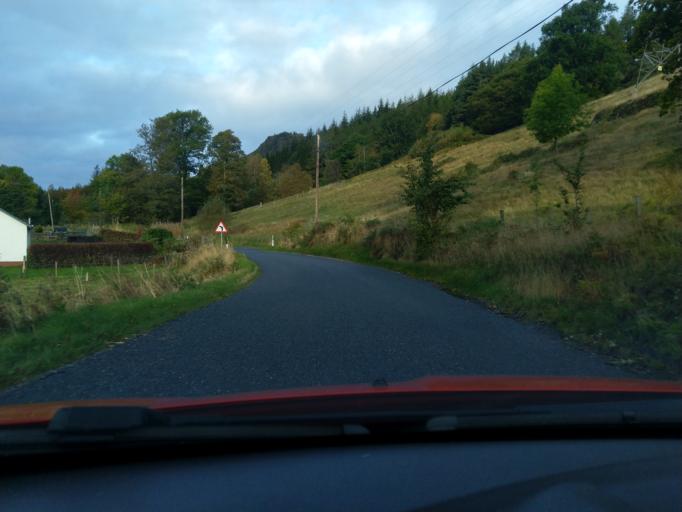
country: GB
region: Scotland
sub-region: Perth and Kinross
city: Aberfeldy
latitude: 56.7018
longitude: -4.1504
